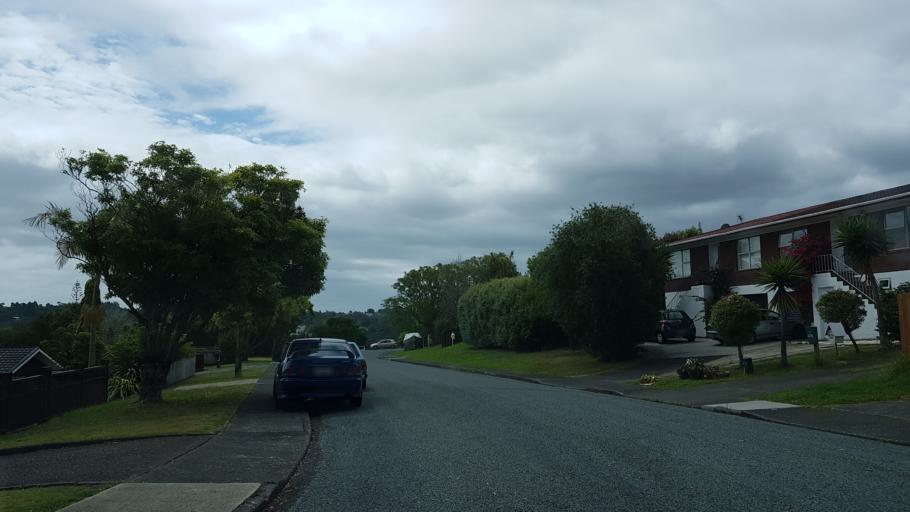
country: NZ
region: Auckland
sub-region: Auckland
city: North Shore
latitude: -36.7763
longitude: 174.7099
